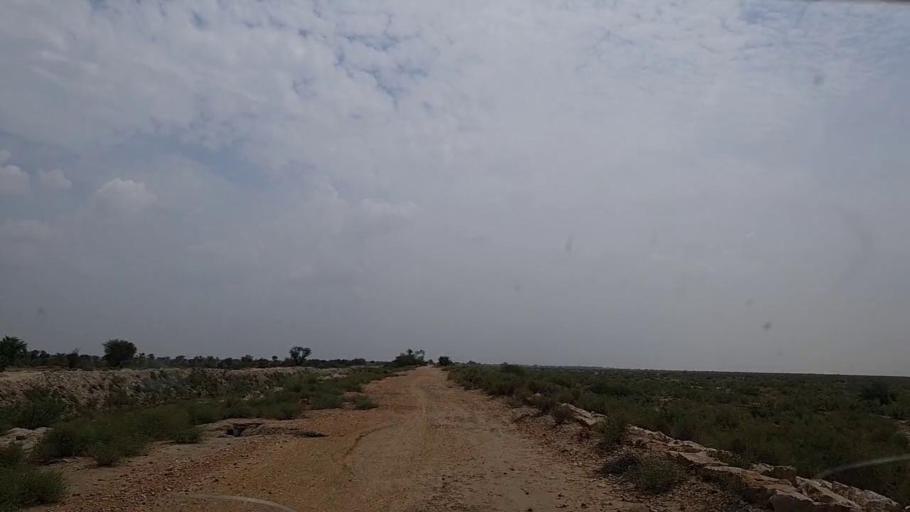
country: PK
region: Sindh
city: Phulji
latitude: 26.8420
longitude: 67.6182
